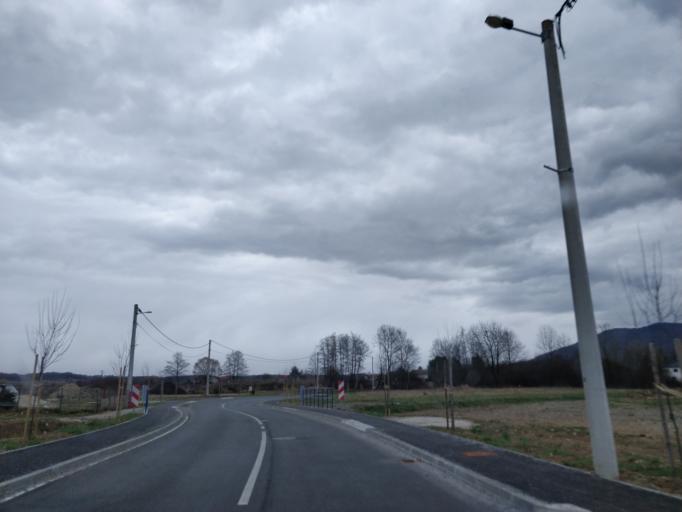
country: HR
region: Zagrebacka
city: Jablanovec
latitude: 45.8981
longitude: 15.8613
